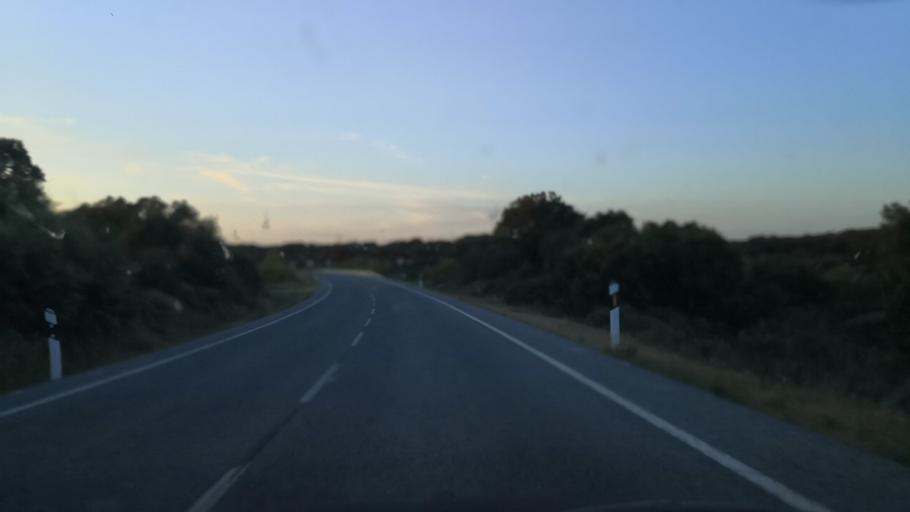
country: ES
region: Extremadura
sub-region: Provincia de Caceres
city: Alcantara
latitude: 39.6826
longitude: -6.8621
